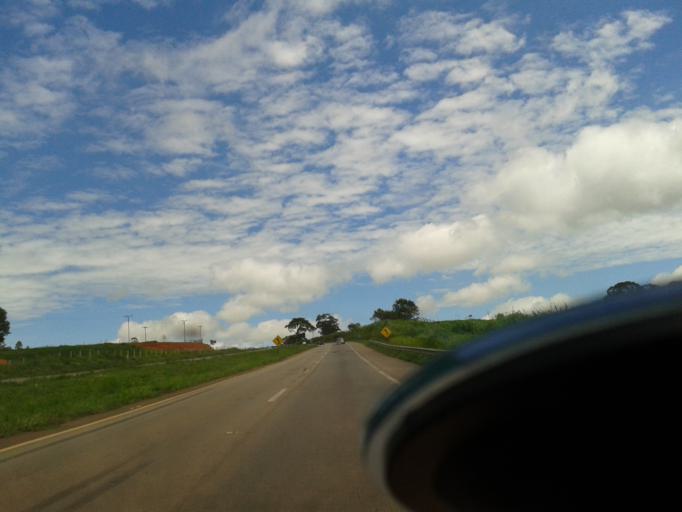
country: BR
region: Goias
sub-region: Inhumas
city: Inhumas
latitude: -16.3157
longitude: -49.5247
